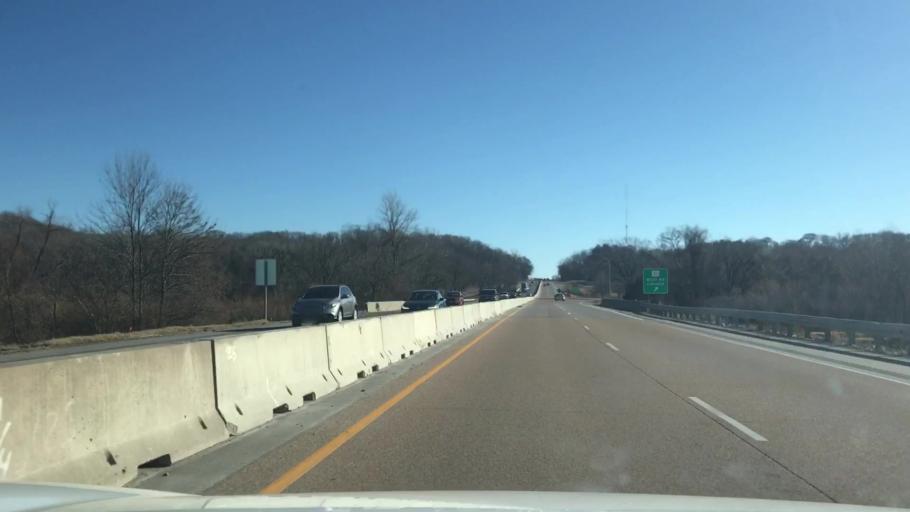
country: US
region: Illinois
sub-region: Saint Clair County
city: Alorton
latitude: 38.5705
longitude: -90.0946
